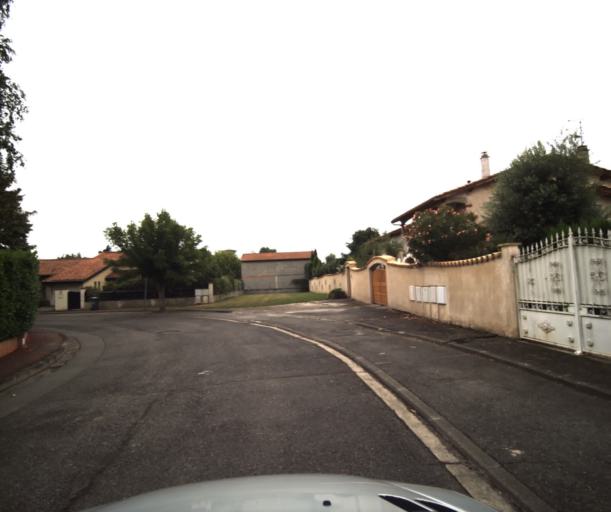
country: FR
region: Midi-Pyrenees
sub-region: Departement de la Haute-Garonne
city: Pinsaguel
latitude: 43.5043
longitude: 1.3923
